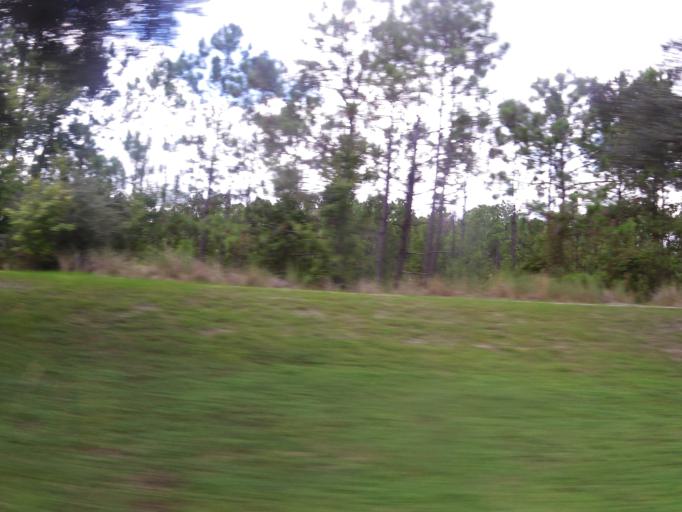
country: US
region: Florida
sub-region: Saint Johns County
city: Villano Beach
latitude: 29.9797
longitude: -81.4710
